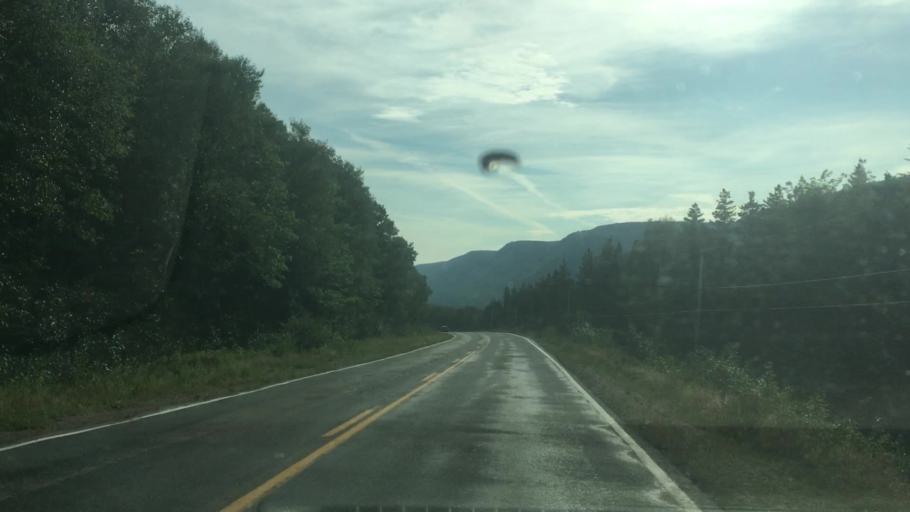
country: CA
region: Nova Scotia
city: Sydney Mines
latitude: 46.8660
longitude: -60.5594
